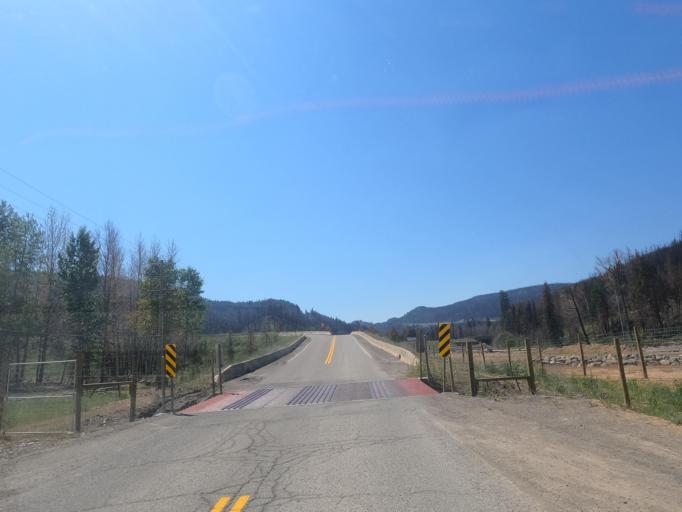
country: CA
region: British Columbia
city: Merritt
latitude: 49.8853
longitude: -120.9033
